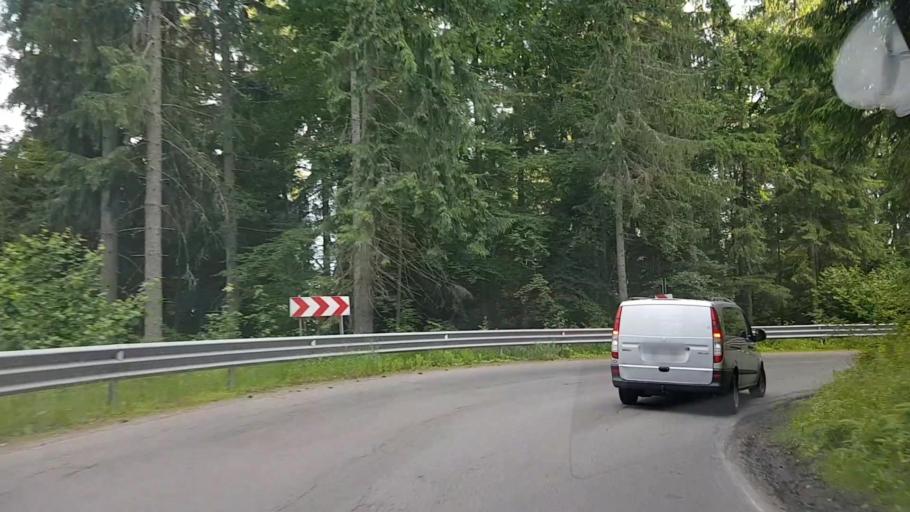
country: RO
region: Harghita
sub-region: Comuna Varsag
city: Varsag
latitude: 46.6714
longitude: 25.3427
